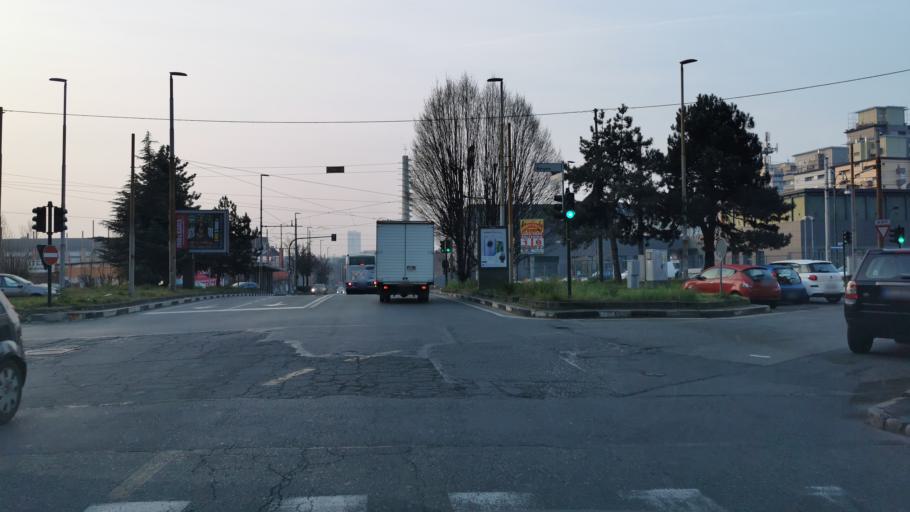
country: IT
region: Piedmont
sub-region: Provincia di Torino
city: Turin
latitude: 45.0958
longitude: 7.6630
